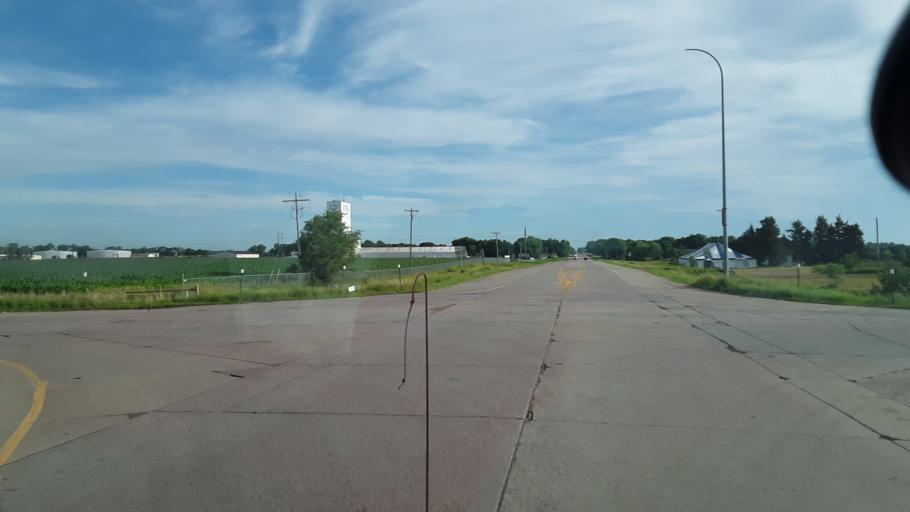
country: US
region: South Dakota
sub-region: Minnehaha County
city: Brandon
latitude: 43.6090
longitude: -96.5722
